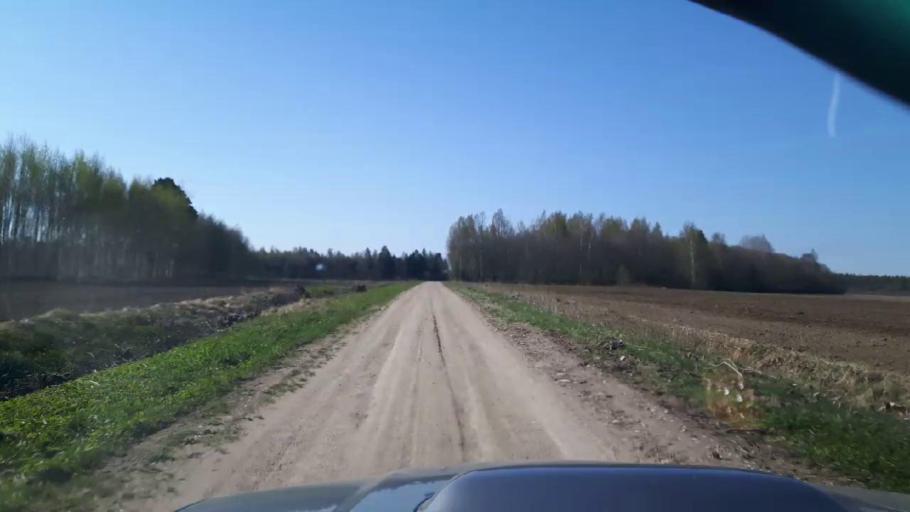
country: EE
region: Paernumaa
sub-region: Tootsi vald
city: Tootsi
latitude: 58.5198
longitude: 24.9291
